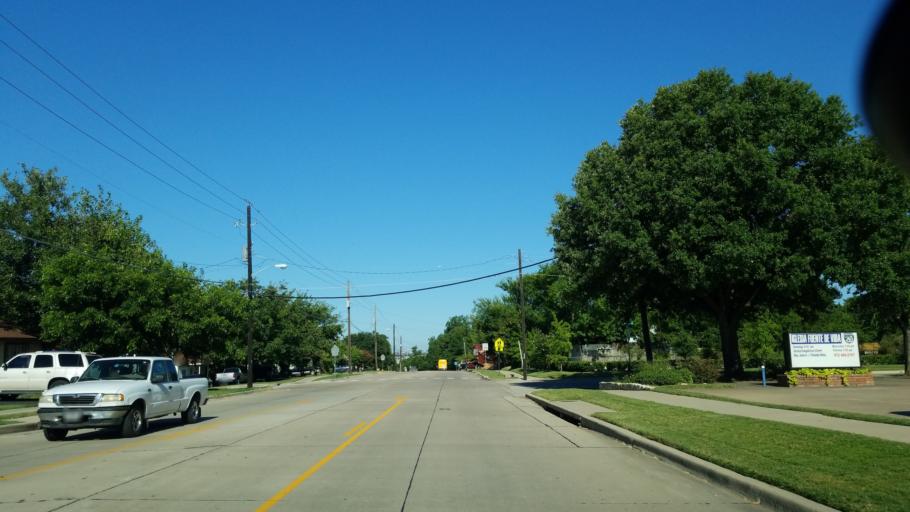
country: US
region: Texas
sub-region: Dallas County
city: Carrollton
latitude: 32.9492
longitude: -96.8969
